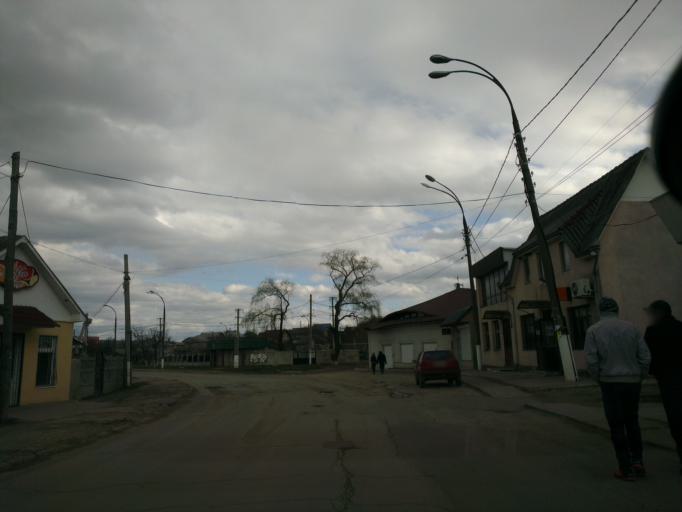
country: MD
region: Hincesti
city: Hincesti
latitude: 46.8201
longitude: 28.5996
